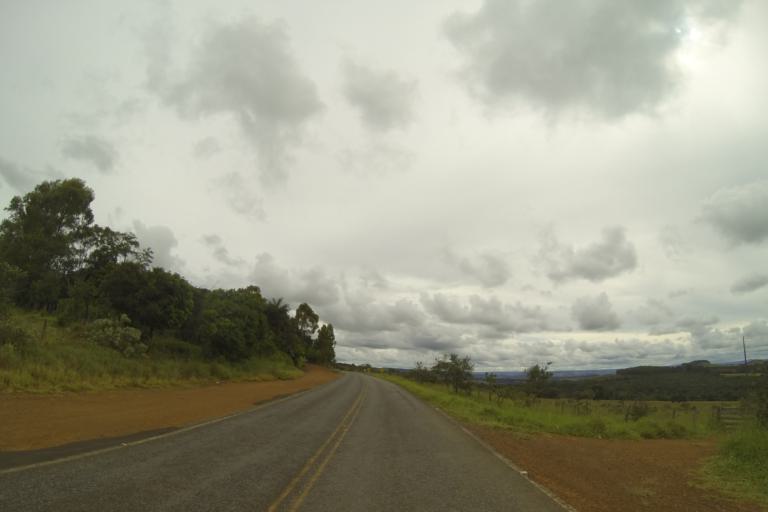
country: BR
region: Minas Gerais
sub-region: Ibia
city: Ibia
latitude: -19.6734
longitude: -46.4398
